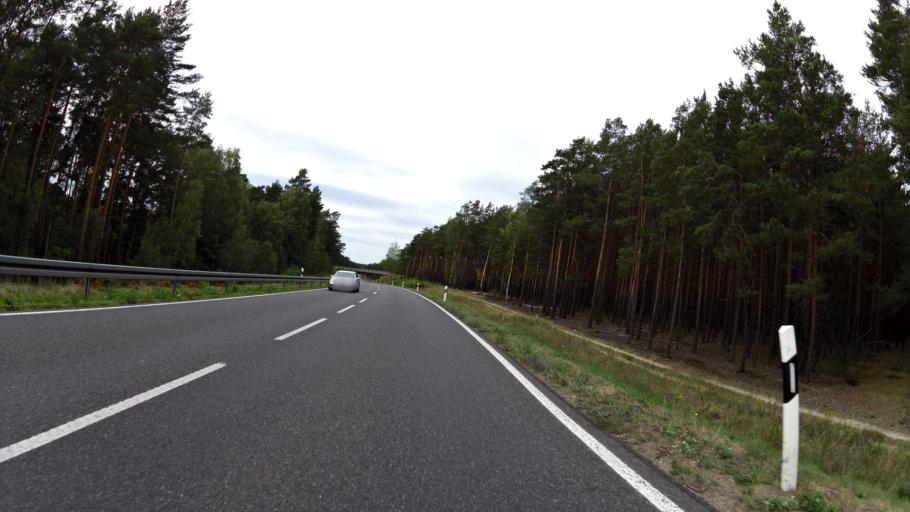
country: DE
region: Brandenburg
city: Schenkendobern
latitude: 51.8945
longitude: 14.6272
